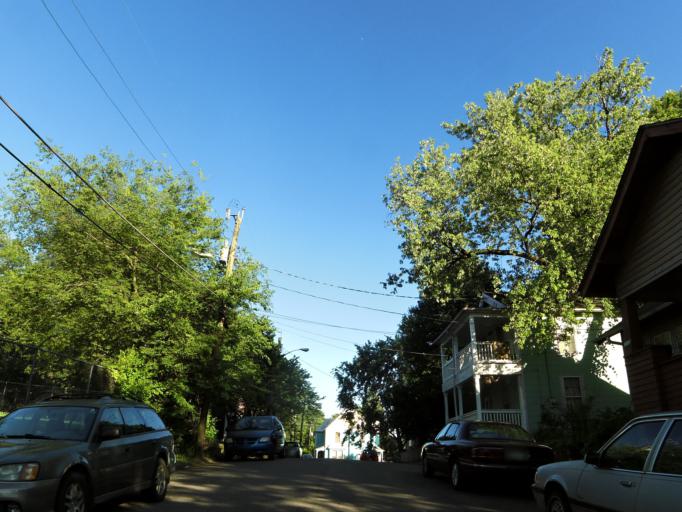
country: US
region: Tennessee
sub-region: Knox County
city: Knoxville
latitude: 35.9681
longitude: -83.9351
